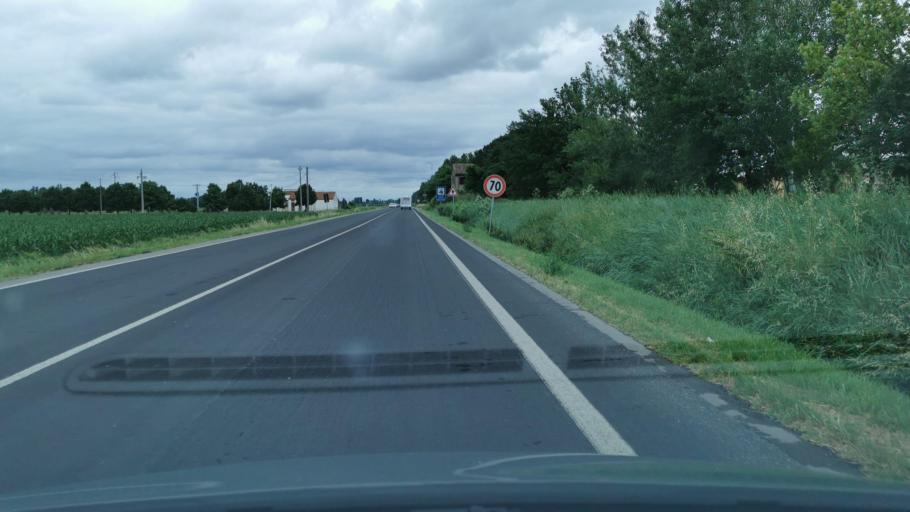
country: IT
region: Emilia-Romagna
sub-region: Provincia di Ravenna
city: Granarolo
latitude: 44.3344
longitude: 11.9150
